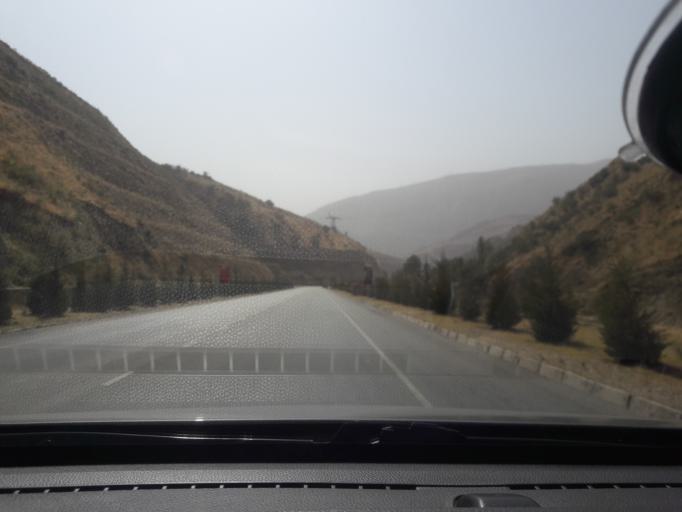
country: TJ
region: Khatlon
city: Norak
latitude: 38.4496
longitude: 69.2020
